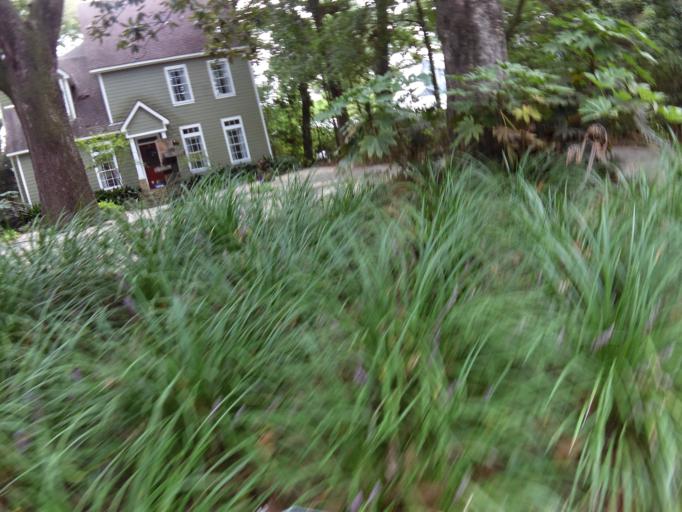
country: US
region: Alabama
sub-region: Baldwin County
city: Fairhope
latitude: 30.5244
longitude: -87.9077
